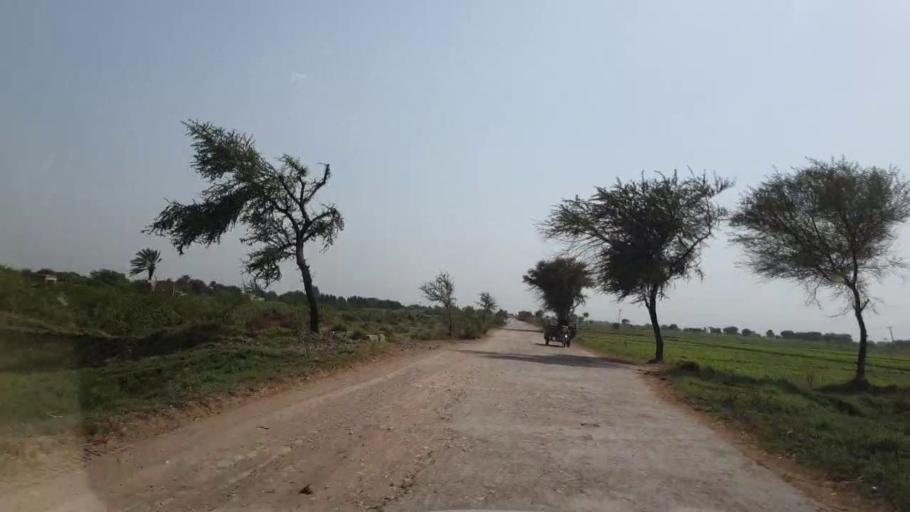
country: PK
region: Sindh
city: Rajo Khanani
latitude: 25.0271
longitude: 68.8730
